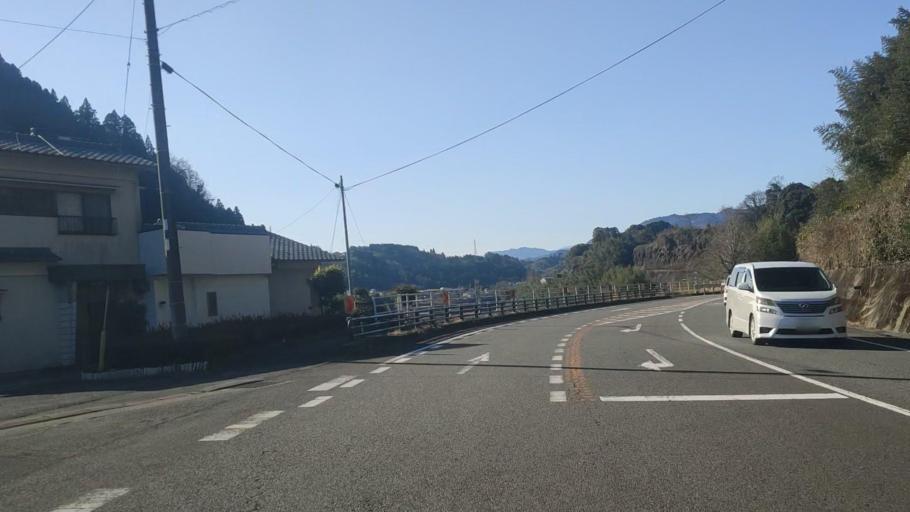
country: JP
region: Oita
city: Usuki
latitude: 33.0696
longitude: 131.6466
